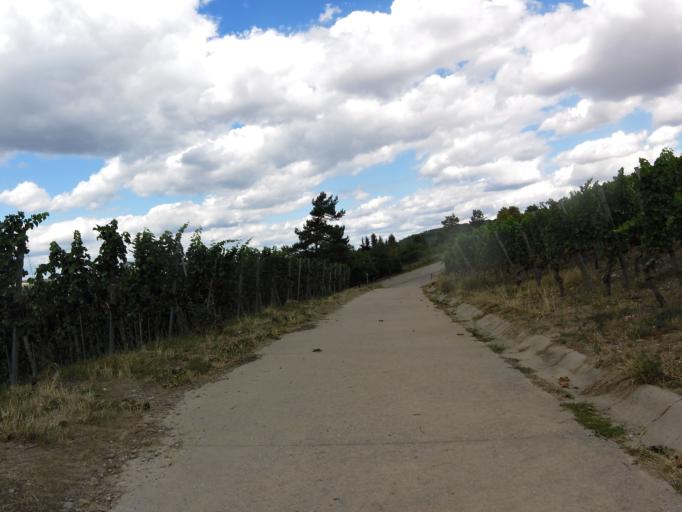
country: DE
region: Bavaria
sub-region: Regierungsbezirk Unterfranken
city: Eibelstadt
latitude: 49.7313
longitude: 9.9975
